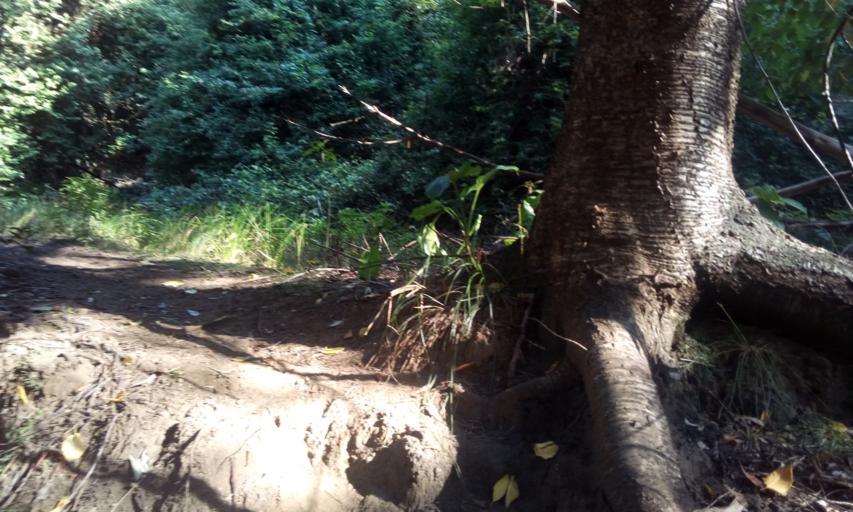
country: AU
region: New South Wales
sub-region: Wollongong
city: Mount Ousley
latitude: -34.3991
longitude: 150.8632
